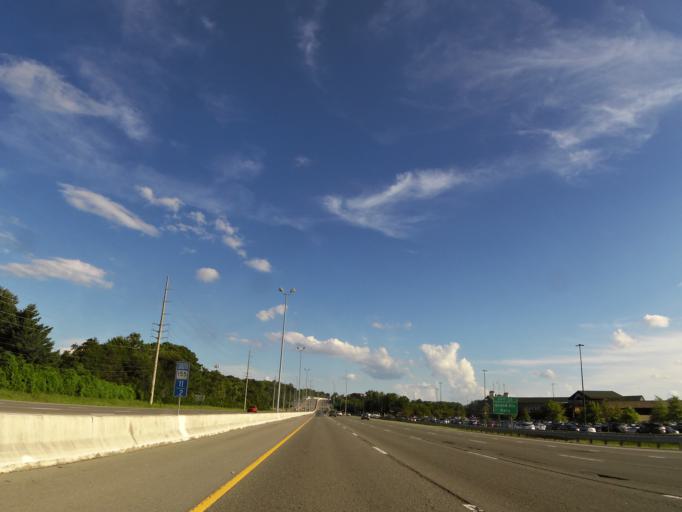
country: US
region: Tennessee
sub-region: Davidson County
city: Lakewood
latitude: 36.2039
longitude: -86.6896
